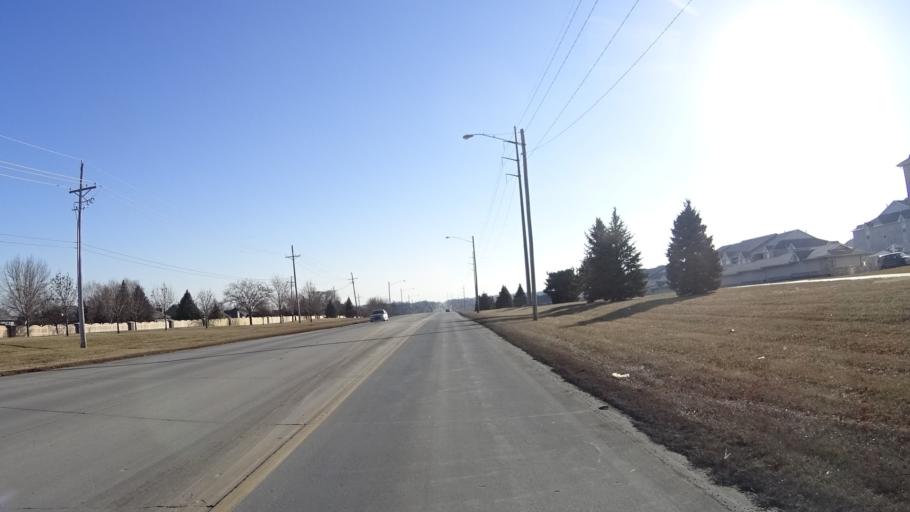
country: US
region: Nebraska
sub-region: Douglas County
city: Bennington
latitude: 41.2984
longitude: -96.1390
